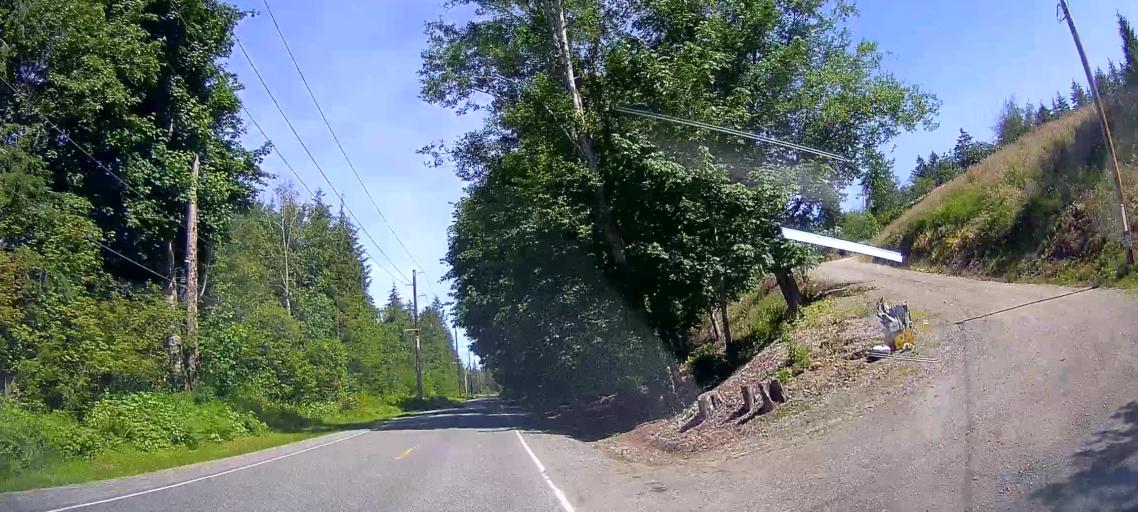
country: US
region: Washington
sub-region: Skagit County
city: Burlington
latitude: 48.5372
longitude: -122.3103
